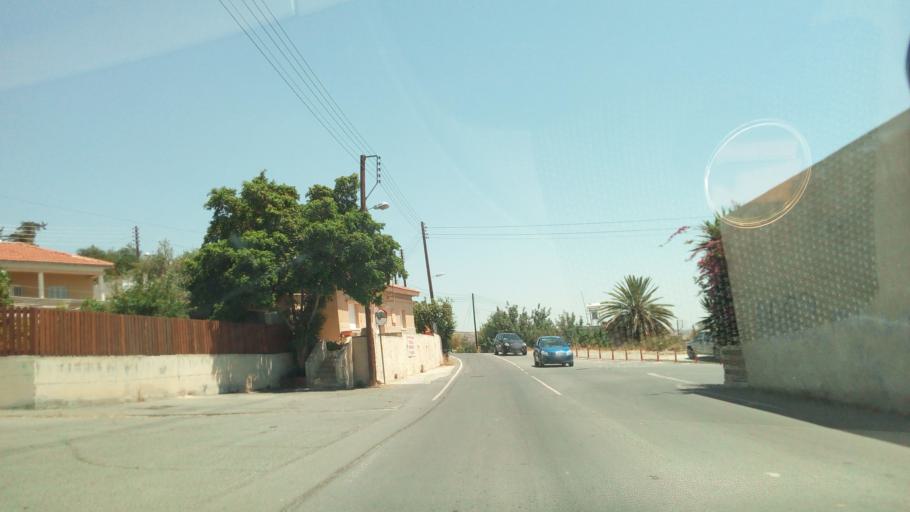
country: CY
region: Limassol
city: Pano Polemidia
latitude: 34.7015
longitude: 33.0004
